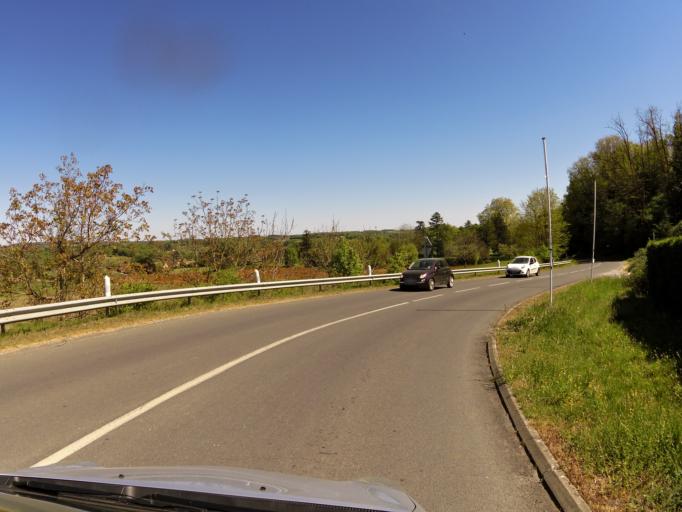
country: FR
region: Aquitaine
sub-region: Departement de la Dordogne
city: Montignac
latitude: 44.9960
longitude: 1.2421
